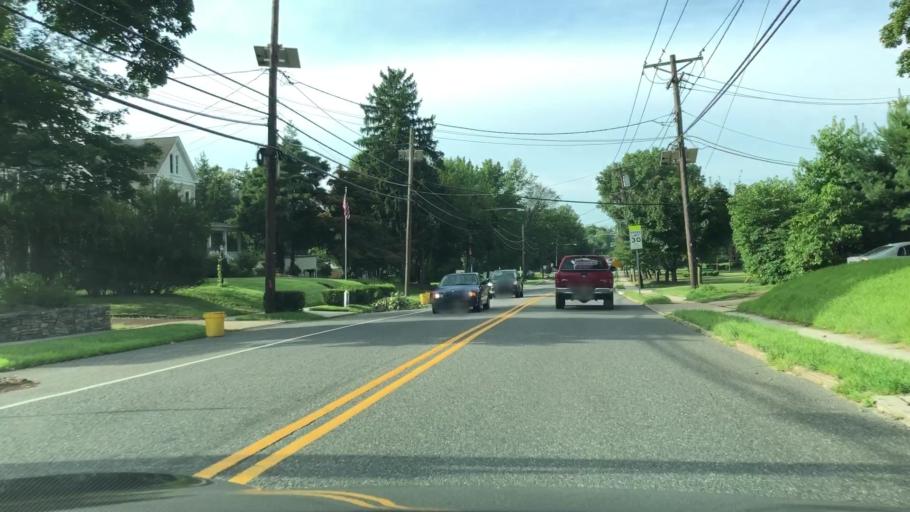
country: US
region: New Jersey
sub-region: Mercer County
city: Prospect Park
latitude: 40.2566
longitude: -74.7419
